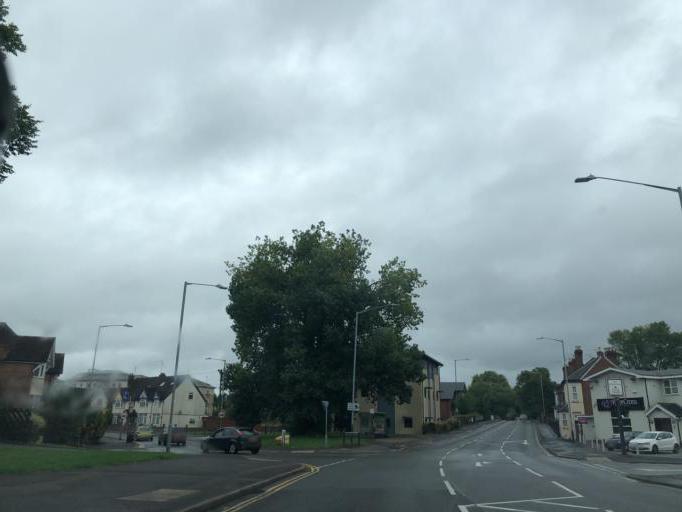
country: GB
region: England
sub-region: Warwickshire
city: Warwick
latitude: 52.2885
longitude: -1.5624
